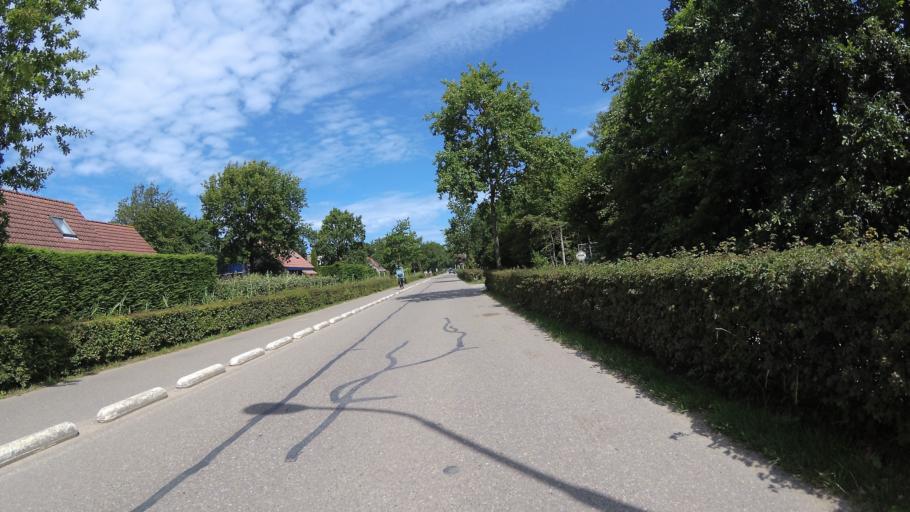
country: NL
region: Zeeland
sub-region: Gemeente Veere
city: Veere
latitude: 51.5836
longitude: 3.6194
